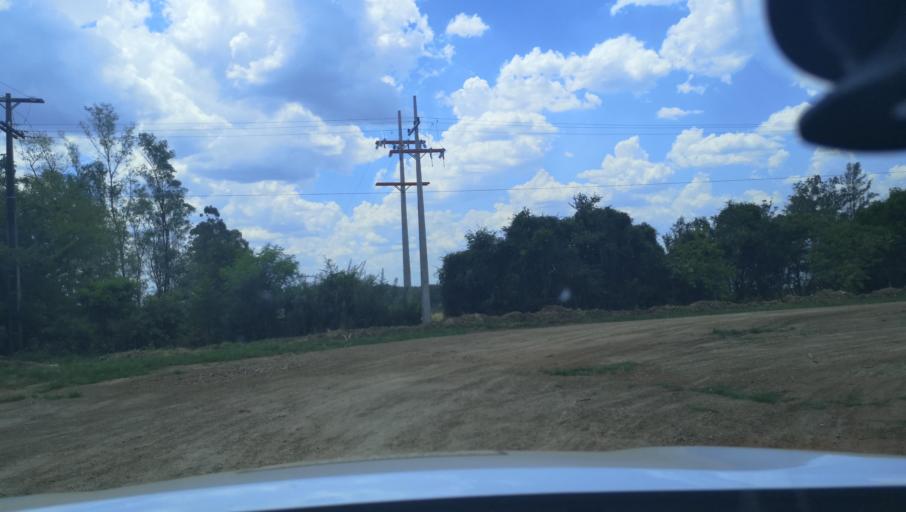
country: PY
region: Itapua
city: Carmen del Parana
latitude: -27.1546
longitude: -56.2500
